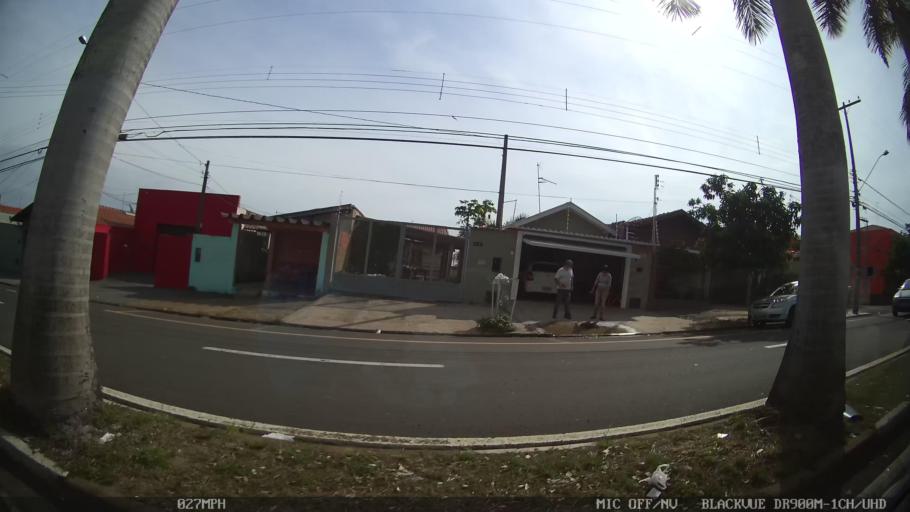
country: BR
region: Sao Paulo
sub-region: Piracicaba
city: Piracicaba
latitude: -22.7376
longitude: -47.6648
